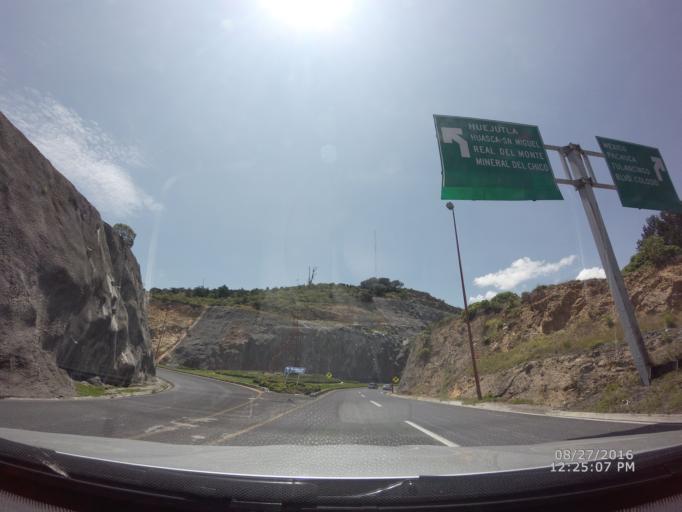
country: MX
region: Hidalgo
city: Mineral del Monte
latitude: 20.1390
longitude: -98.6908
